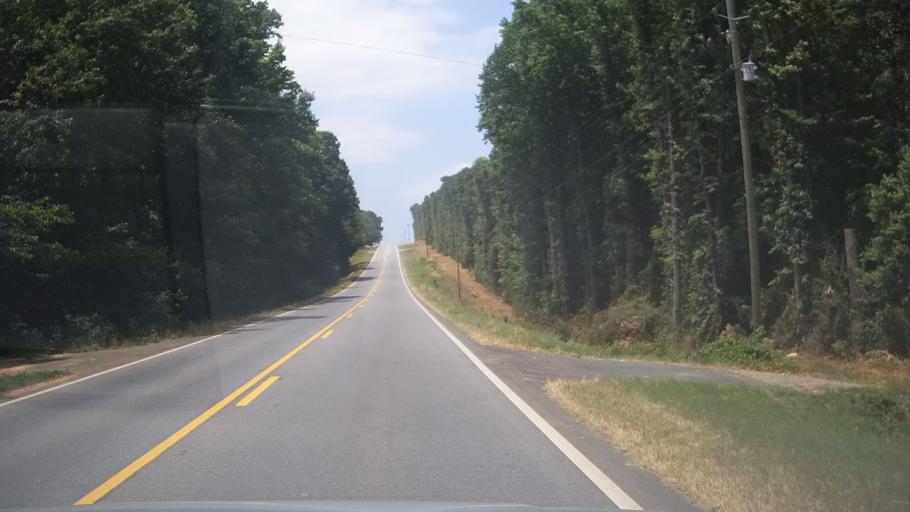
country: US
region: Georgia
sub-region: Madison County
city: Danielsville
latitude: 34.1780
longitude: -83.3203
